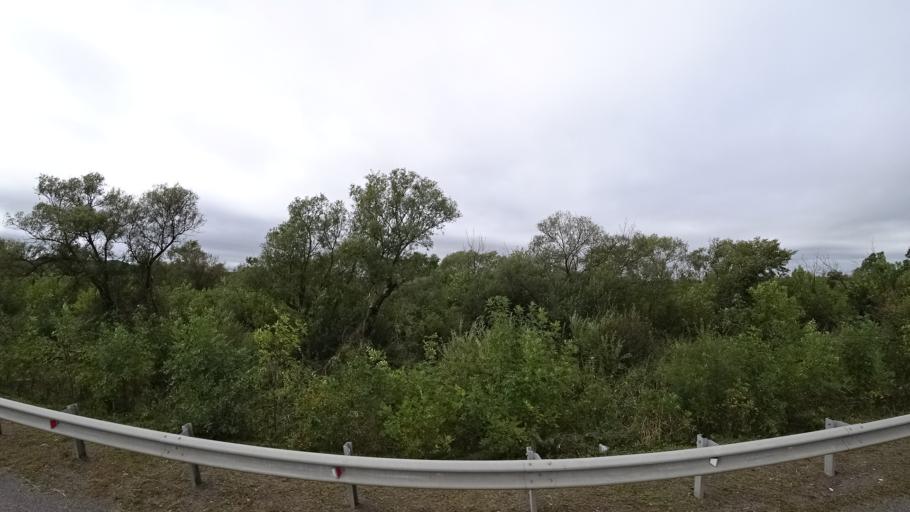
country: RU
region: Primorskiy
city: Monastyrishche
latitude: 44.1821
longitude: 132.4415
